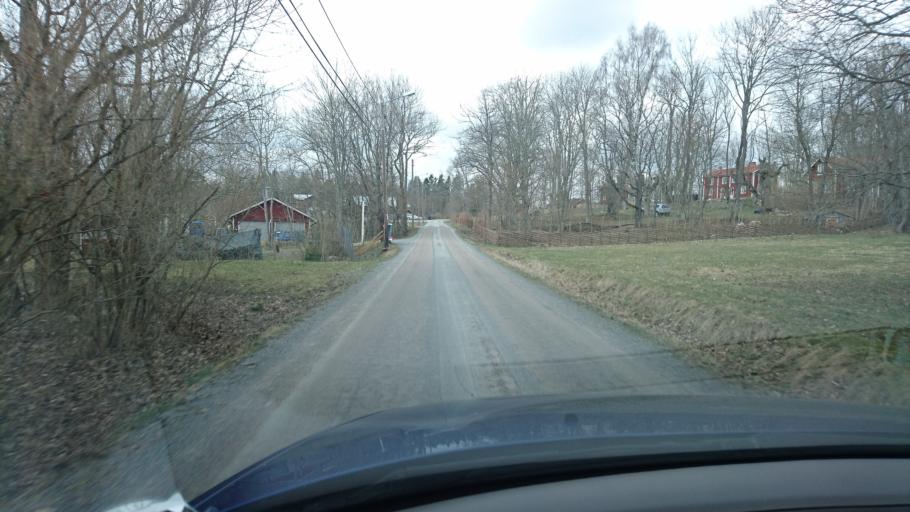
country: SE
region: Stockholm
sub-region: Norrtalje Kommun
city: Bjorko
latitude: 59.7854
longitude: 18.9449
